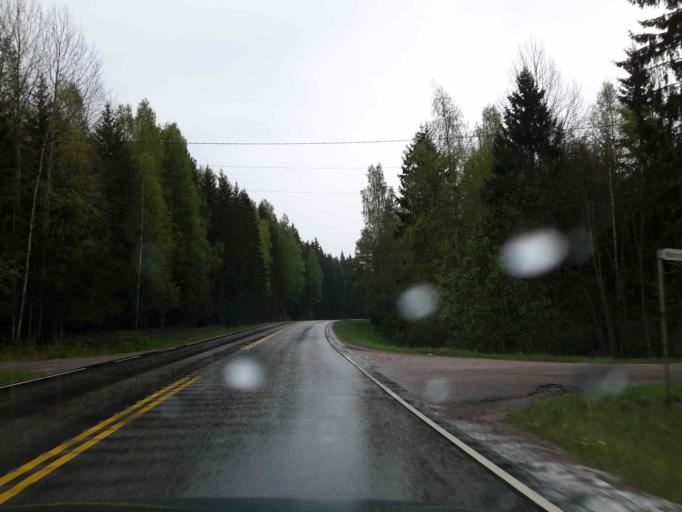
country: FI
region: Uusimaa
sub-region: Helsinki
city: Vihti
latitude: 60.3885
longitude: 24.5062
